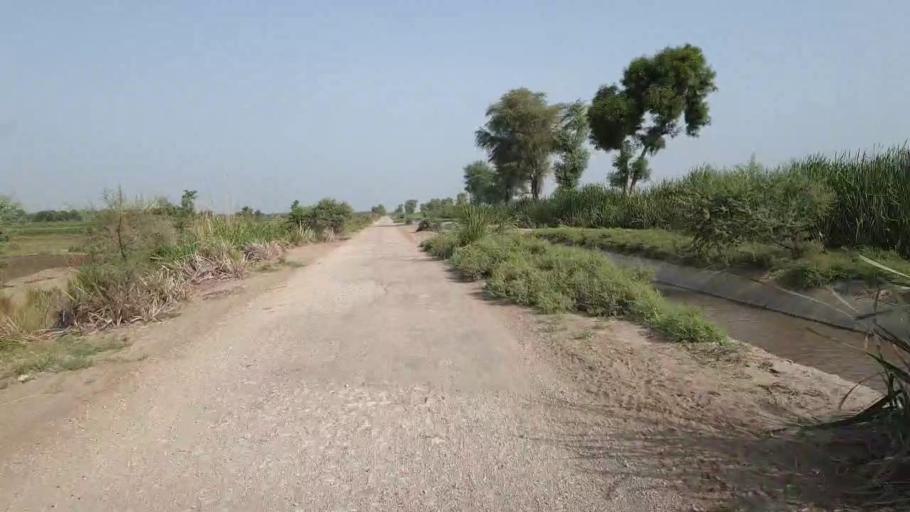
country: PK
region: Sindh
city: Daur
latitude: 26.3401
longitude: 68.1825
